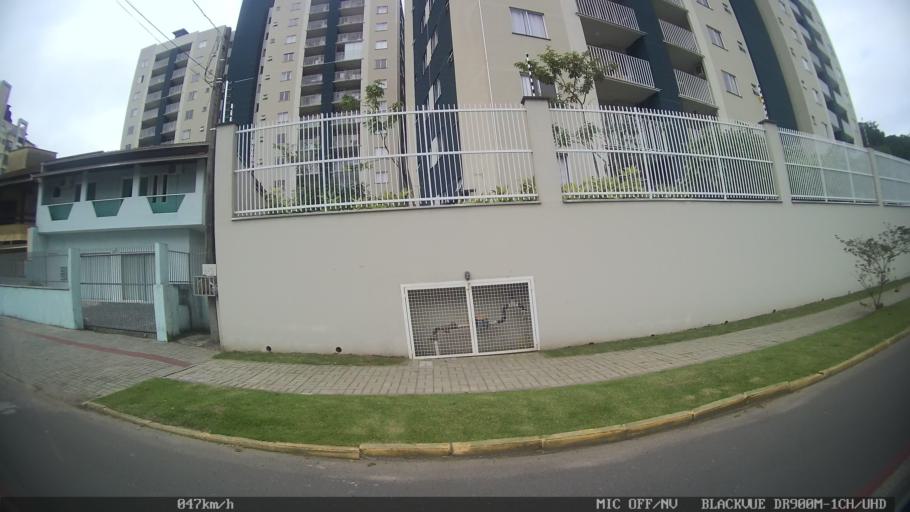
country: BR
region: Santa Catarina
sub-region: Joinville
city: Joinville
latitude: -26.3185
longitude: -48.8623
